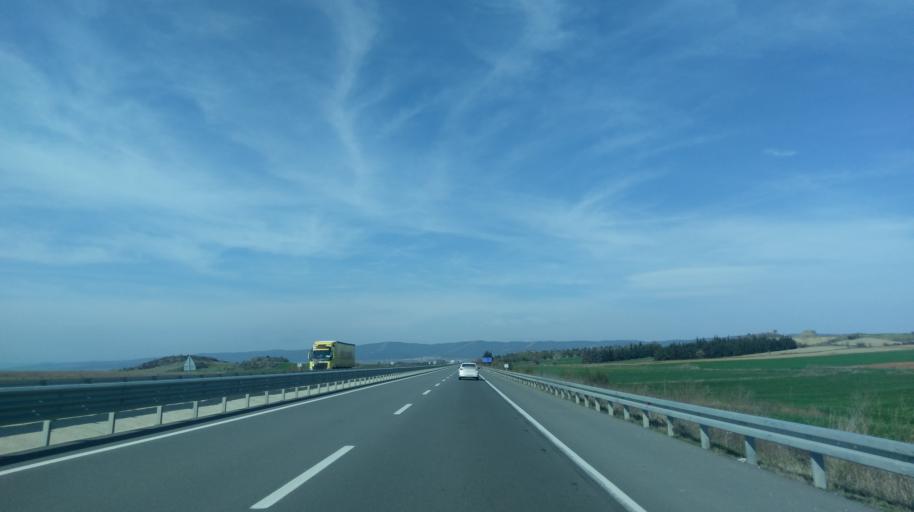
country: TR
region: Canakkale
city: Evrese
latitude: 40.6420
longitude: 26.8535
